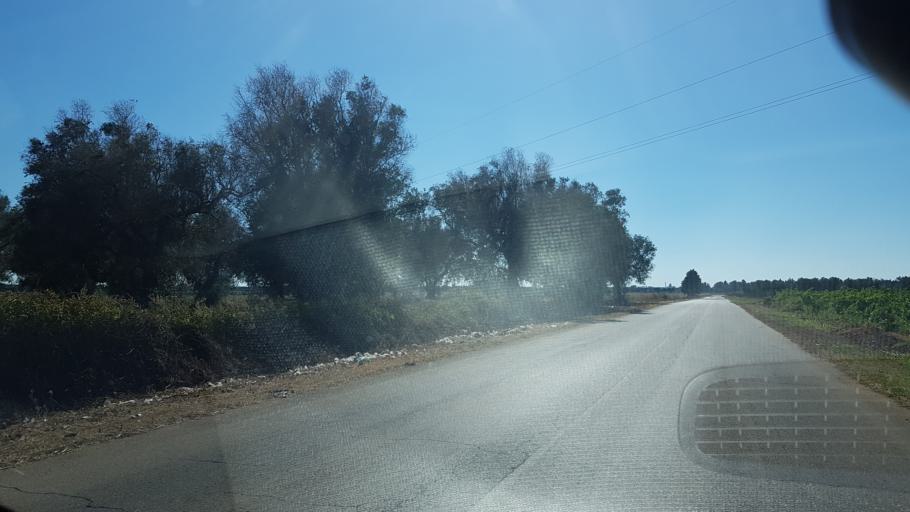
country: IT
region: Apulia
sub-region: Provincia di Brindisi
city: Mesagne
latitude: 40.5564
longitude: 17.8573
